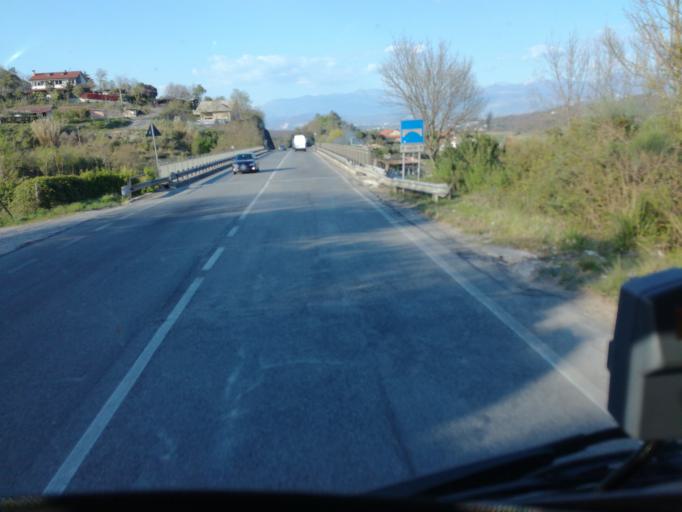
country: IT
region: Latium
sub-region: Provincia di Frosinone
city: Giuliano di Roma
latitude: 41.5616
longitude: 13.2672
